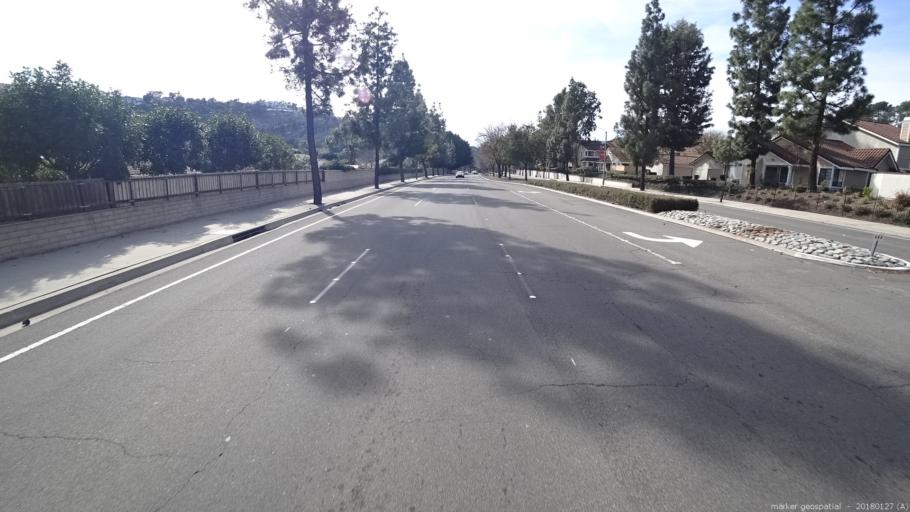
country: US
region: California
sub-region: Los Angeles County
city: Diamond Bar
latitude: 33.9943
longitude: -117.8150
